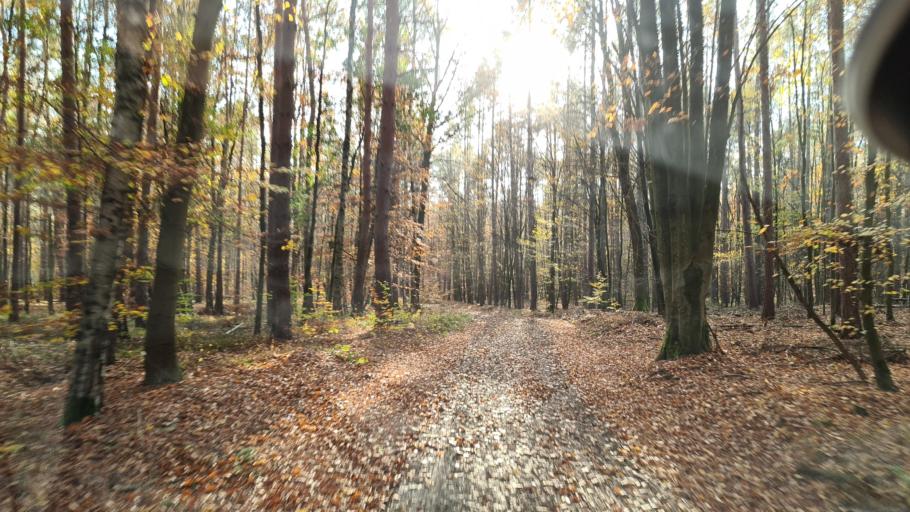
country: DE
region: Saxony
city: Dahlen
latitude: 51.4143
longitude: 13.0041
